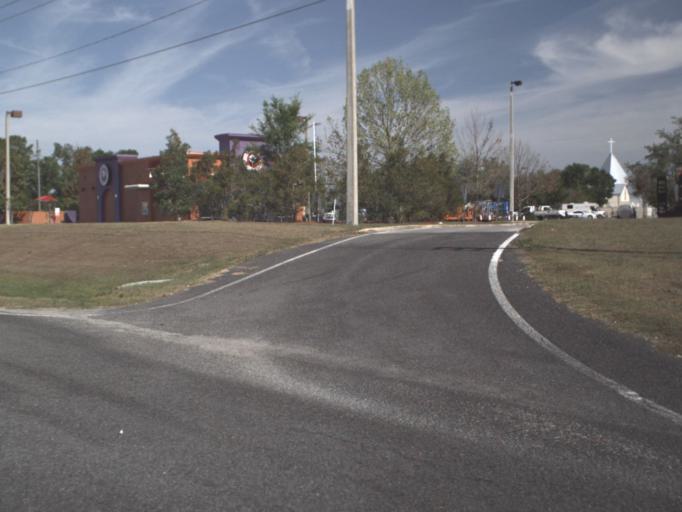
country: US
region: Florida
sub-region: Lake County
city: Lady Lake
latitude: 28.9342
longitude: -81.9358
